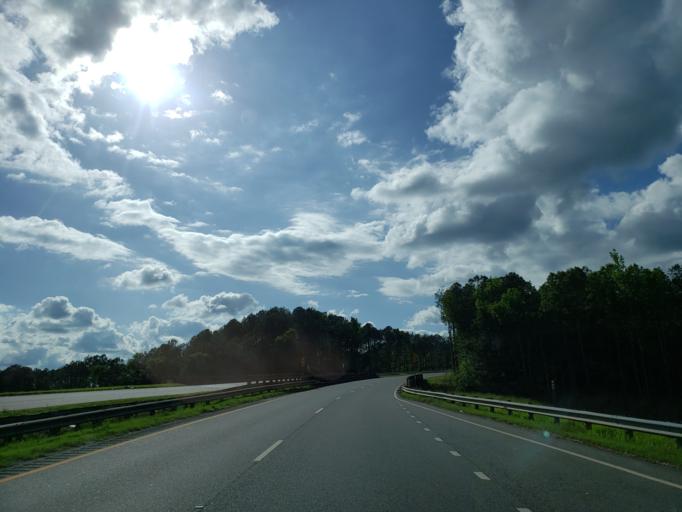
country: US
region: Georgia
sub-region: Bartow County
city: Cartersville
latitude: 34.2208
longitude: -84.8497
